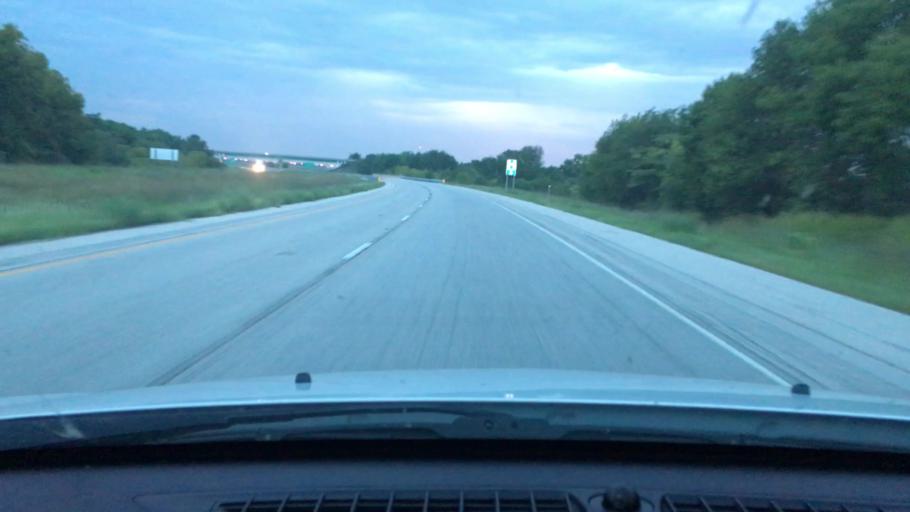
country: US
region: Illinois
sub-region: Morgan County
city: Jacksonville
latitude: 39.7371
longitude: -90.1507
